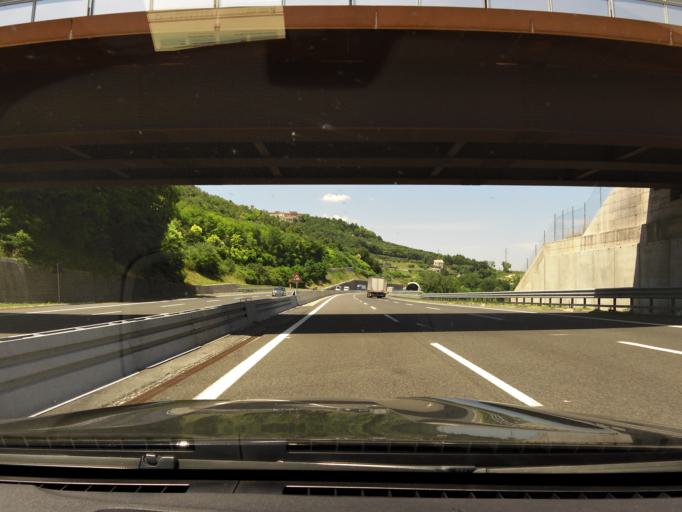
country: IT
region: The Marches
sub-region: Provincia di Pesaro e Urbino
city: Fenile
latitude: 43.8587
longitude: 12.9408
